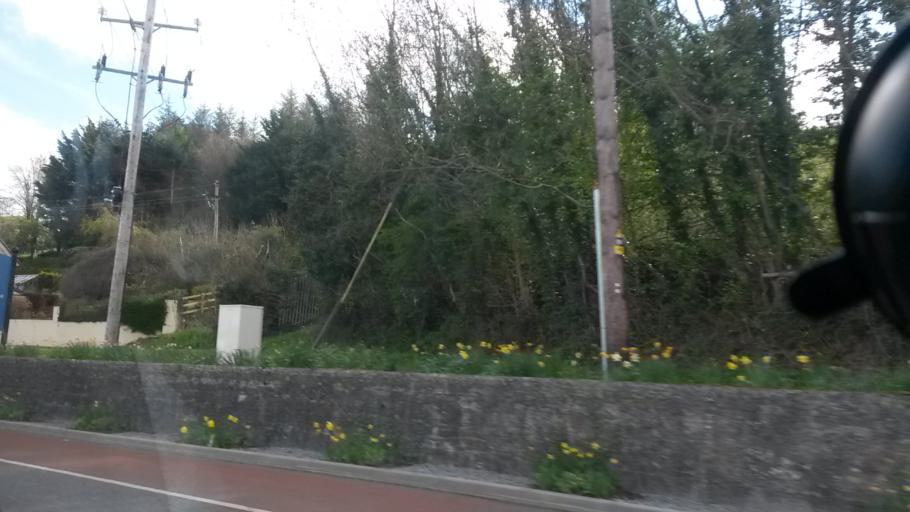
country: IE
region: Ulster
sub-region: An Cabhan
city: Cavan
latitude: 53.9984
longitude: -7.3554
